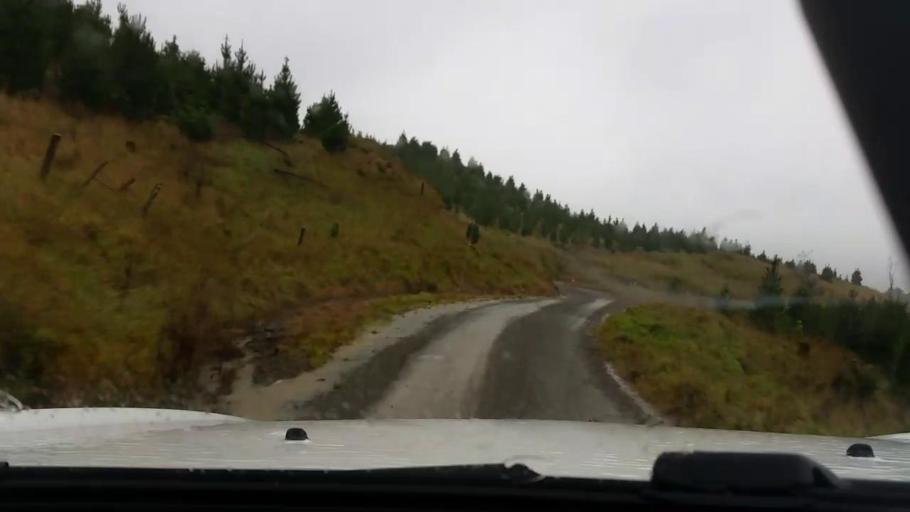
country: NZ
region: Wellington
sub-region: Masterton District
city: Masterton
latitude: -41.1980
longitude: 175.8112
